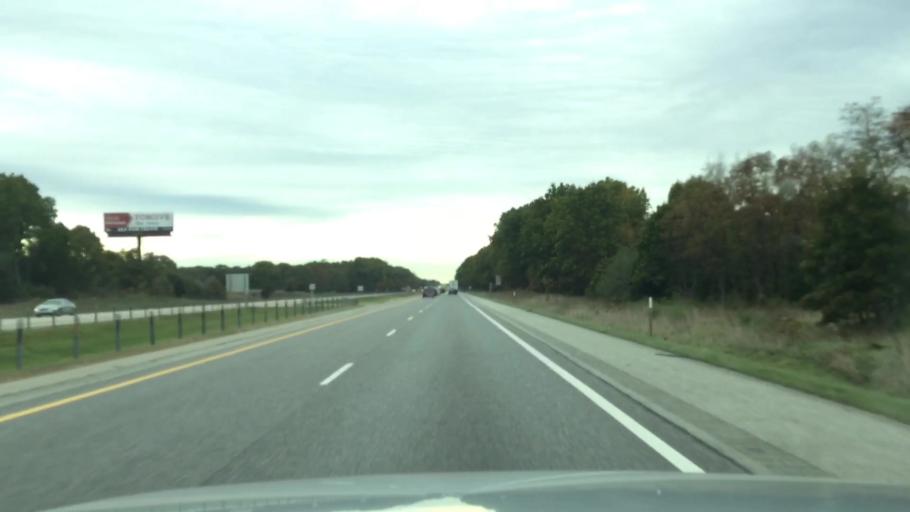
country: US
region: Michigan
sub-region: Van Buren County
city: Mattawan
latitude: 42.2223
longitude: -85.7956
